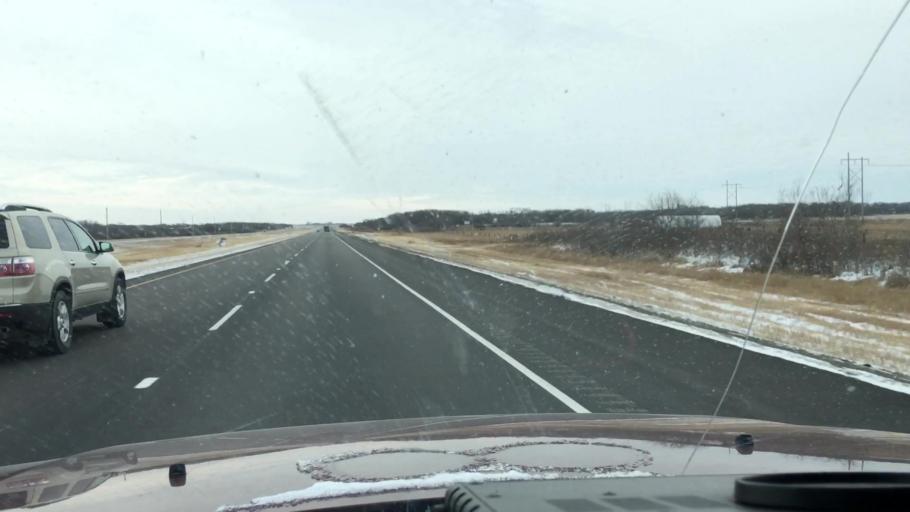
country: CA
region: Saskatchewan
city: Saskatoon
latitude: 51.8849
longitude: -106.5144
